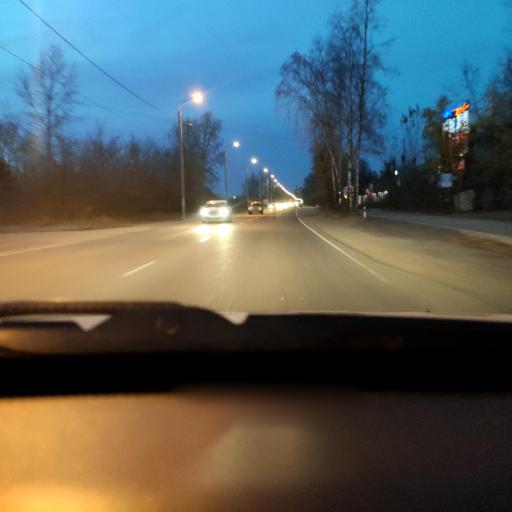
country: RU
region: Perm
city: Kondratovo
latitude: 57.9724
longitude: 56.1281
